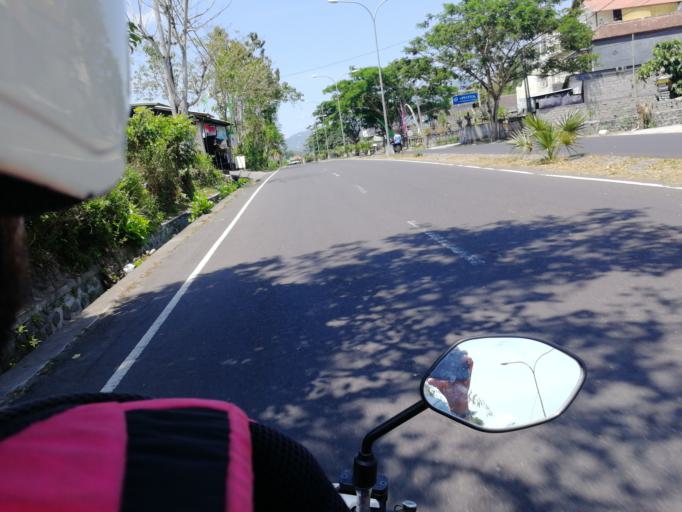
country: ID
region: Bali
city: Subagan
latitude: -8.4404
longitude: 115.5922
